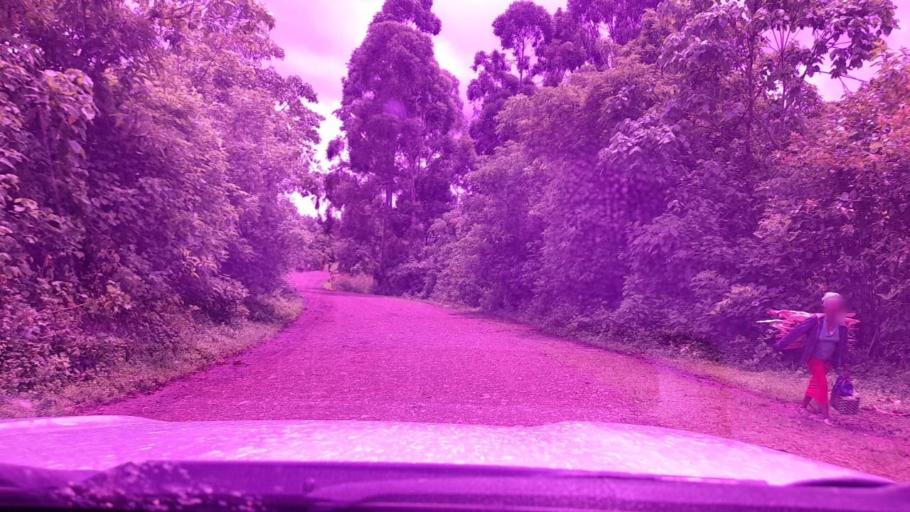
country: ET
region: Southern Nations, Nationalities, and People's Region
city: Tippi
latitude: 7.6201
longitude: 35.5837
